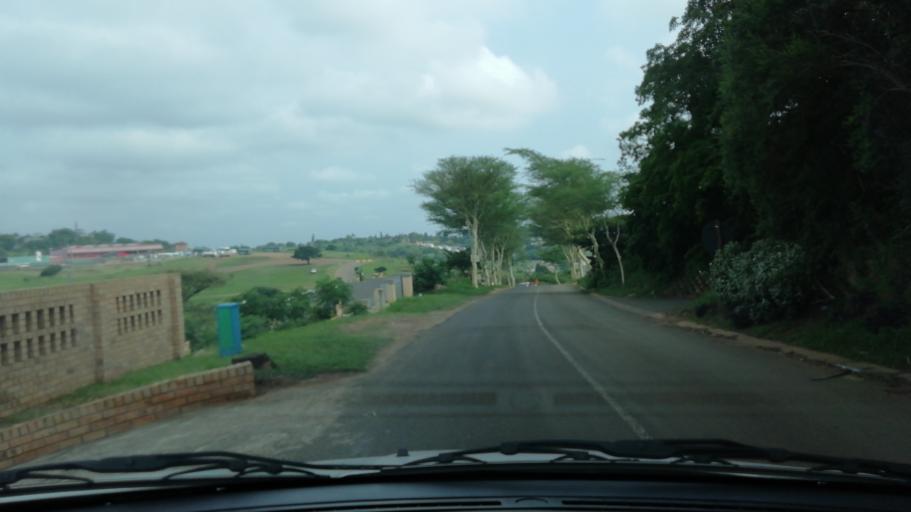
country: ZA
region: KwaZulu-Natal
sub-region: uThungulu District Municipality
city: Empangeni
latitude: -28.7413
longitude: 31.8801
